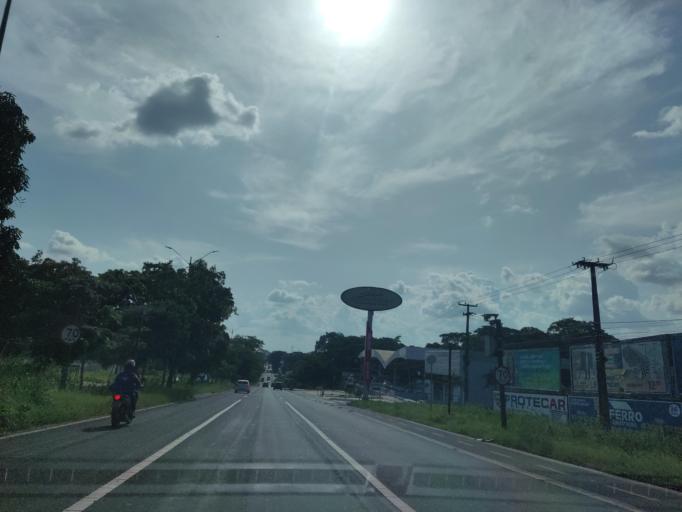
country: BR
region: Piaui
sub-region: Teresina
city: Teresina
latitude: -5.0790
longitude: -42.7528
